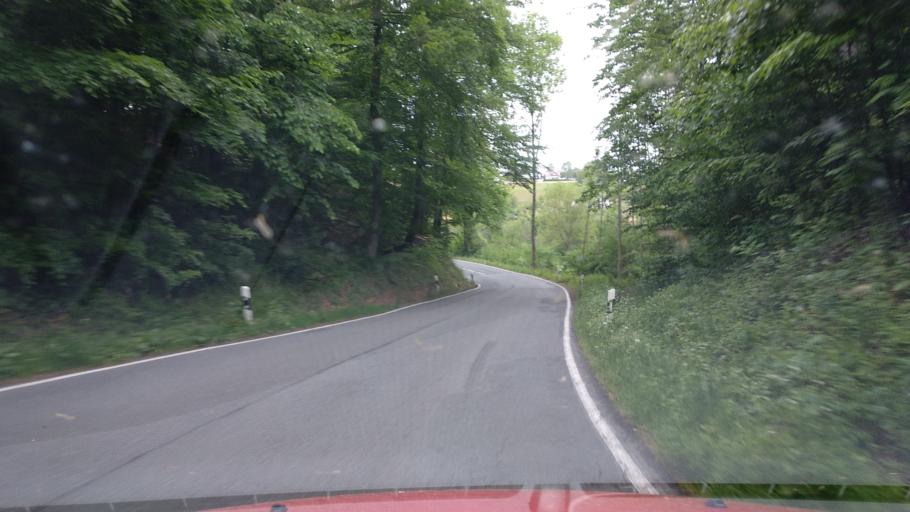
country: DE
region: North Rhine-Westphalia
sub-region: Regierungsbezirk Detmold
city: Willebadessen
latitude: 51.6208
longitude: 9.1011
